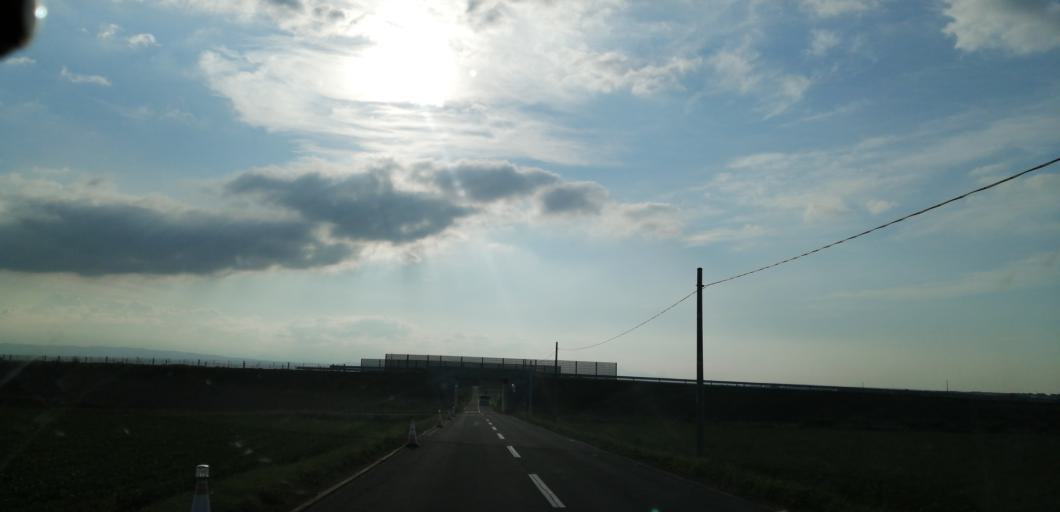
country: JP
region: Hokkaido
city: Chitose
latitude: 42.9353
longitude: 141.7170
